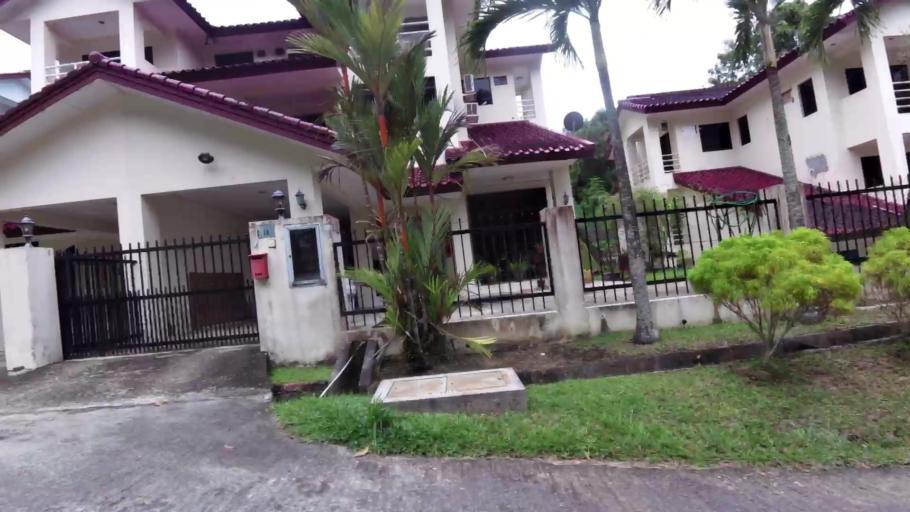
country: BN
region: Brunei and Muara
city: Bandar Seri Begawan
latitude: 4.8884
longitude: 114.9243
